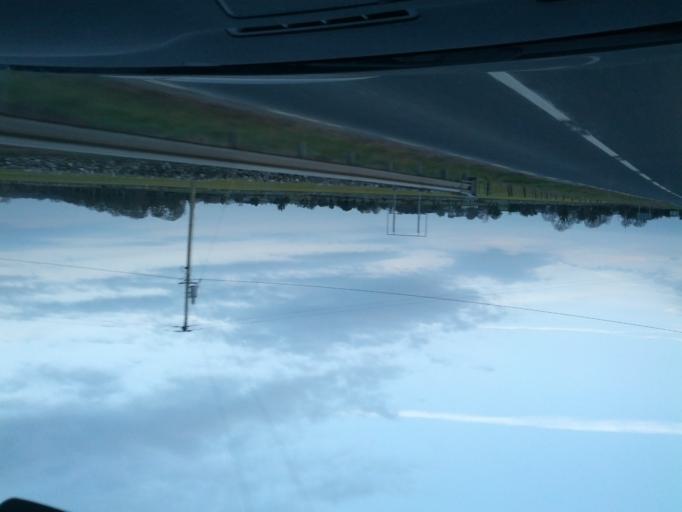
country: IE
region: Connaught
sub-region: County Galway
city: Portumna
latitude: 53.0182
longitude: -8.1254
